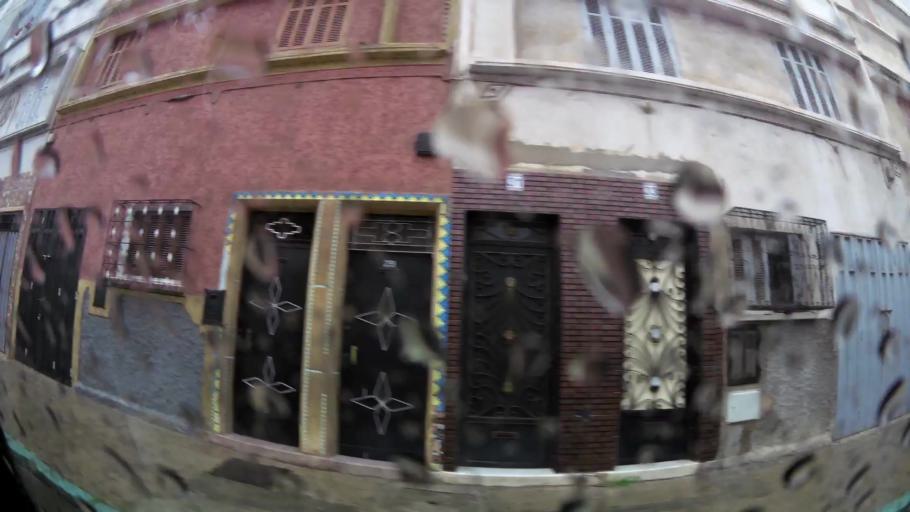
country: MA
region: Grand Casablanca
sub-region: Casablanca
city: Casablanca
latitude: 33.5450
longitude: -7.5693
